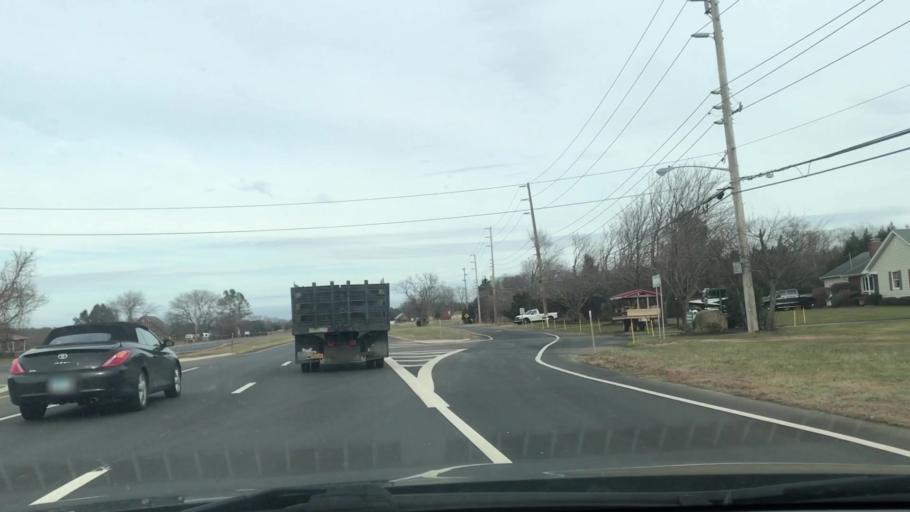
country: US
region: New York
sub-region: Suffolk County
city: Southold
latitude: 41.0549
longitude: -72.4532
